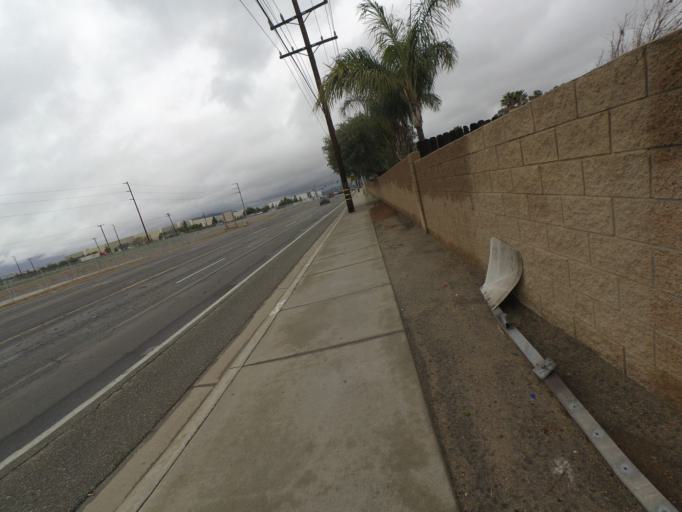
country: US
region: California
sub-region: Riverside County
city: March Air Force Base
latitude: 33.9082
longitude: -117.2436
